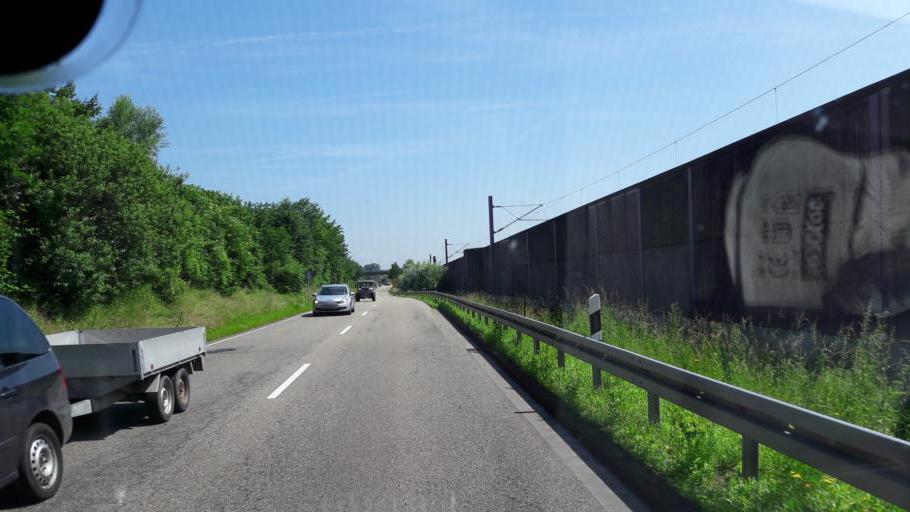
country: DE
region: Baden-Wuerttemberg
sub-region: Karlsruhe Region
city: Sinzheim
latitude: 48.7748
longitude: 8.1738
